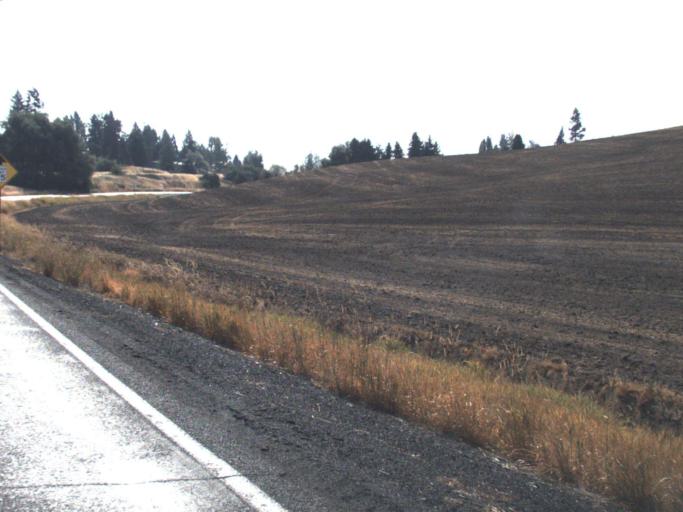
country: US
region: Washington
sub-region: Whitman County
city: Colfax
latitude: 47.0158
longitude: -117.1456
